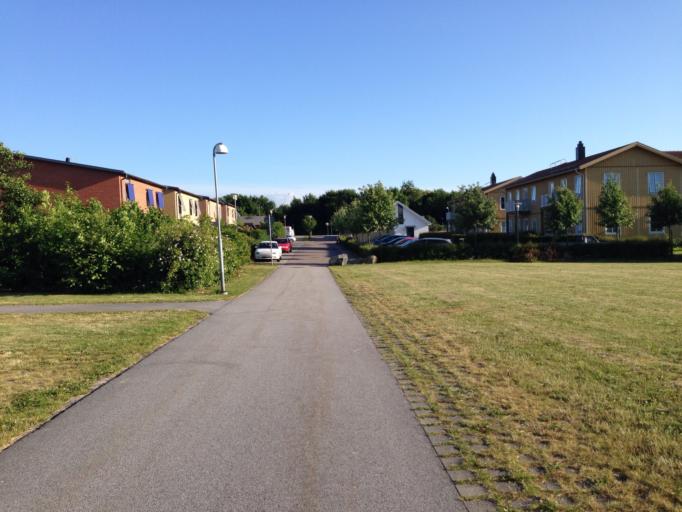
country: SE
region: Skane
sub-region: Lomma Kommun
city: Lomma
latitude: 55.6758
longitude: 13.0927
